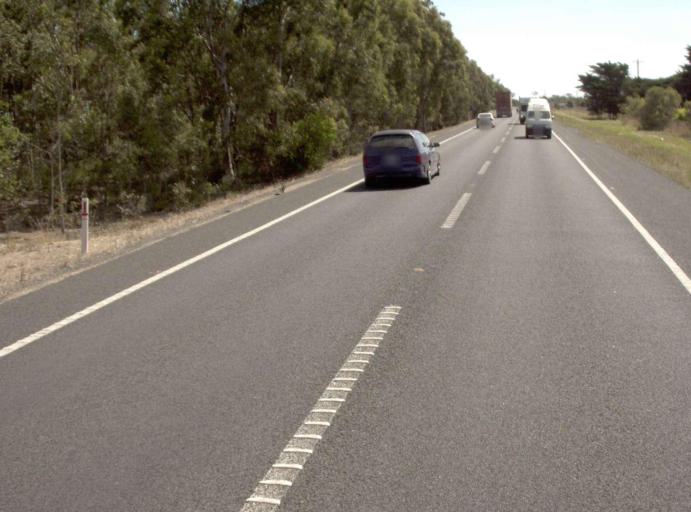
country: AU
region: Victoria
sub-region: East Gippsland
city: Bairnsdale
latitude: -37.8454
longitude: 147.5738
